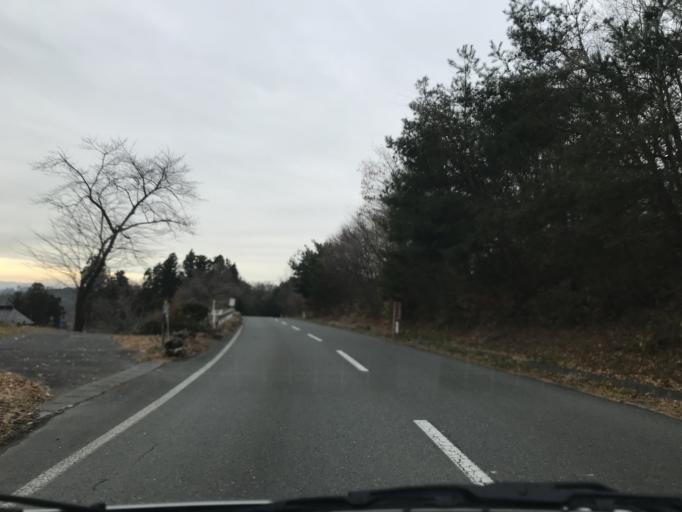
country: JP
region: Iwate
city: Ichinoseki
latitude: 38.7728
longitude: 141.2410
